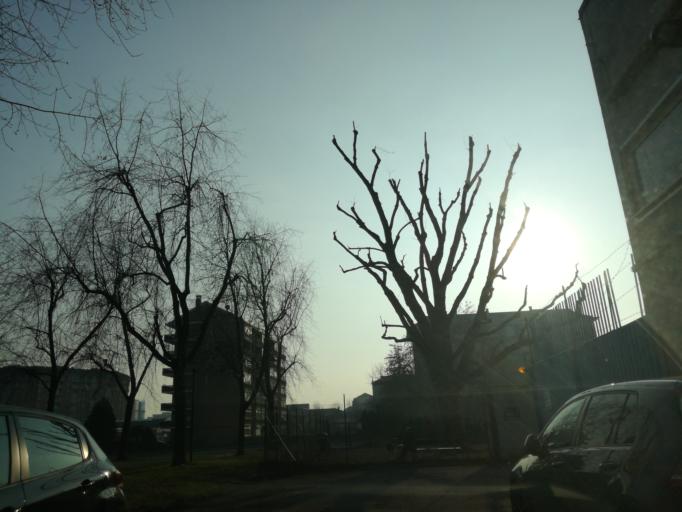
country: IT
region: Piedmont
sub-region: Provincia di Torino
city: Gerbido
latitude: 45.0473
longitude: 7.6186
